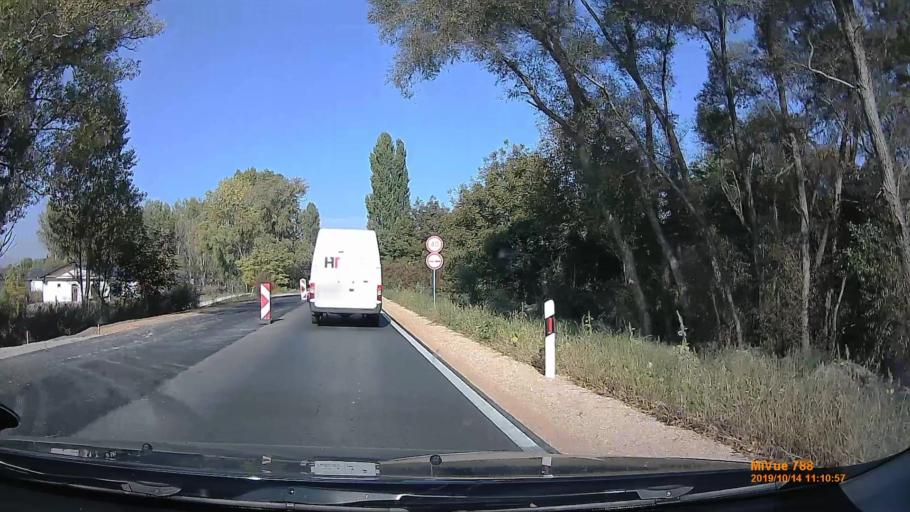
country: HU
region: Pest
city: Peteri
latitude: 47.3772
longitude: 19.4200
